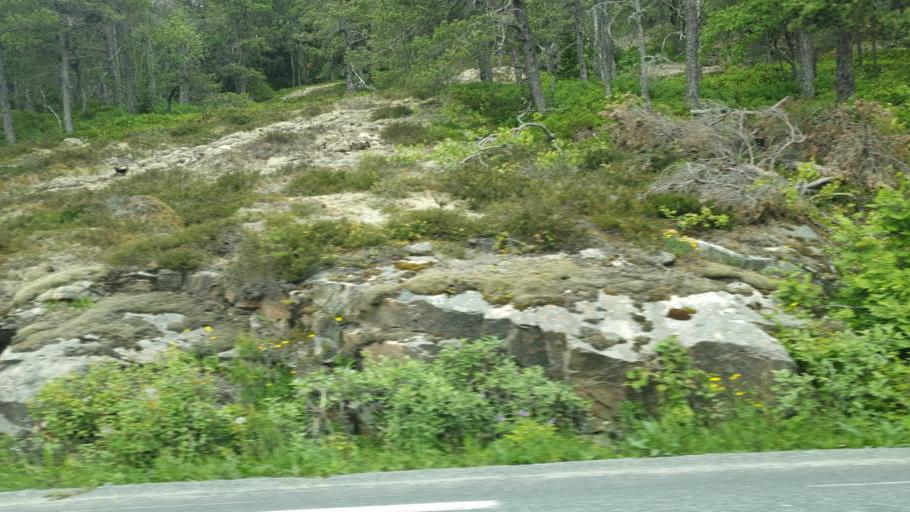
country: NO
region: Sor-Trondelag
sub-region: Trondheim
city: Trondheim
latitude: 63.5566
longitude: 10.3083
